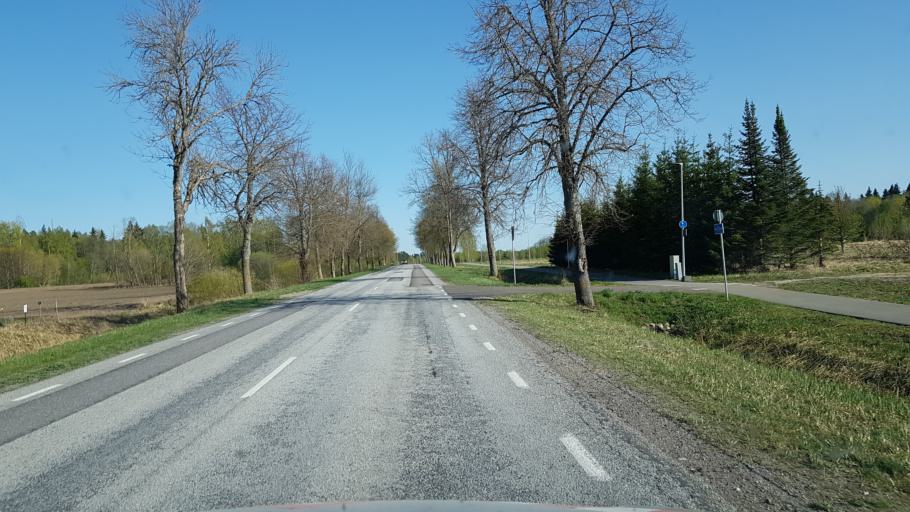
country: EE
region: Paernumaa
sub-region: Paikuse vald
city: Paikuse
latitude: 58.3626
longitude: 24.6490
